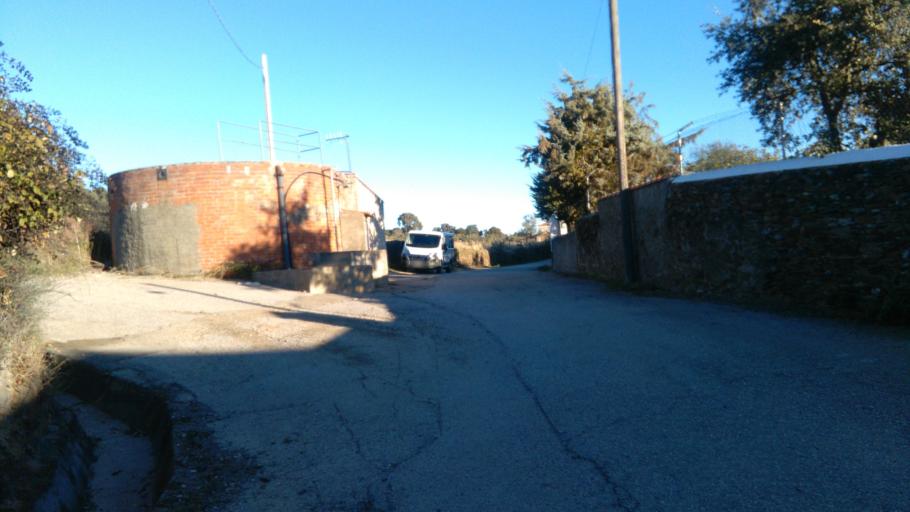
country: ES
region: Extremadura
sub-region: Provincia de Caceres
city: Herguijuela
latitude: 39.3955
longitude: -5.7846
